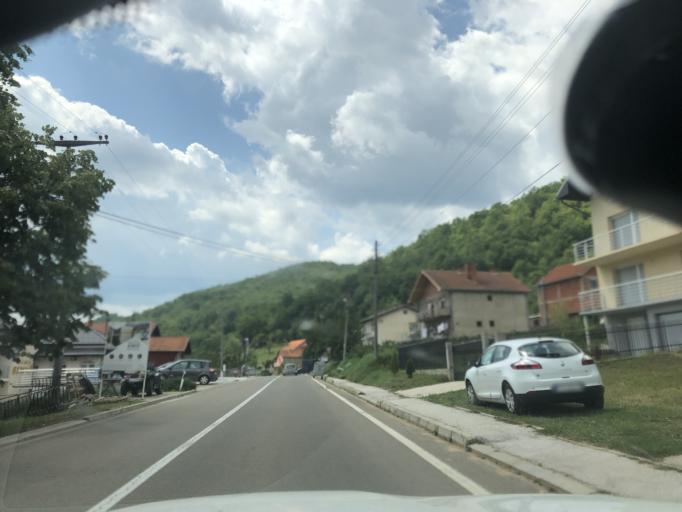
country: RS
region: Central Serbia
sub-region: Jablanicki Okrug
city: Medvega
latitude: 42.8304
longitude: 21.5837
